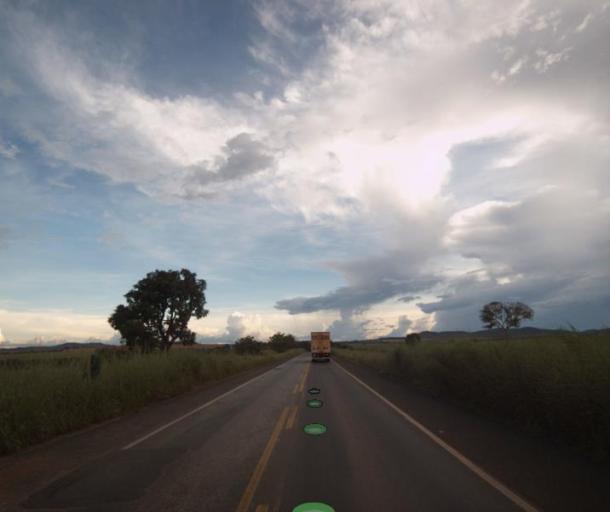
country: BR
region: Goias
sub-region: Uruacu
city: Uruacu
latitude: -14.1211
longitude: -49.1076
